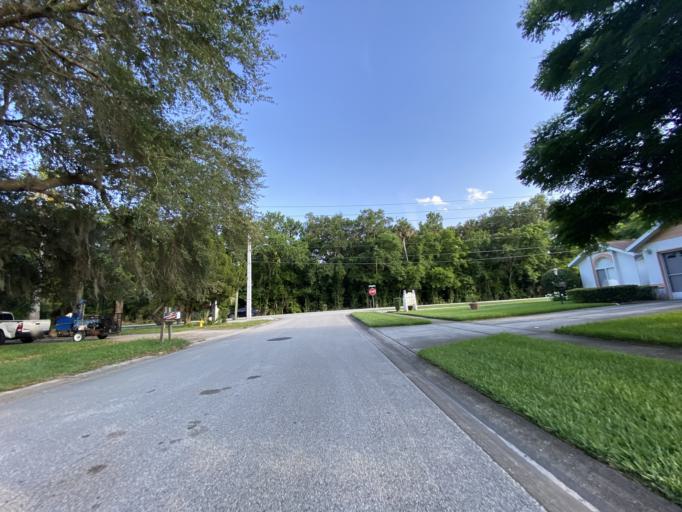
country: US
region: Florida
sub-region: Volusia County
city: Port Orange
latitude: 29.1463
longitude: -81.0113
